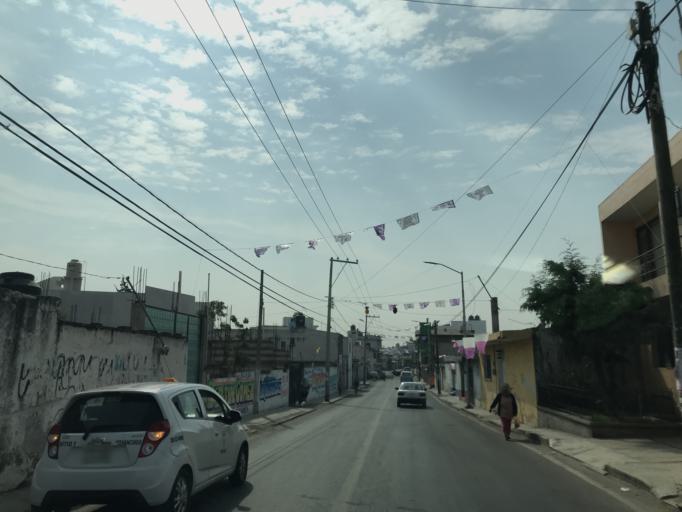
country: MX
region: Tlaxcala
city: Tenancingo
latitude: 19.1475
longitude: -98.2005
